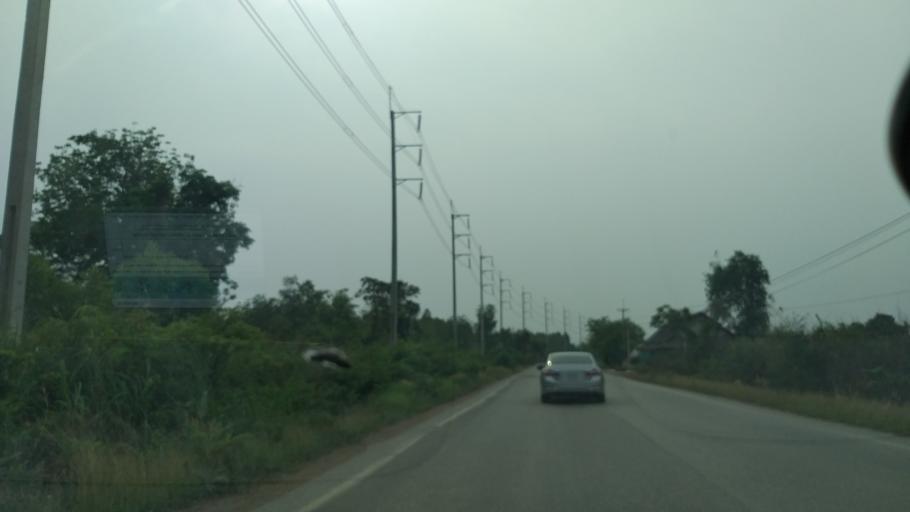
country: TH
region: Chachoengsao
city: Plaeng Yao
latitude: 13.5760
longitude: 101.2466
